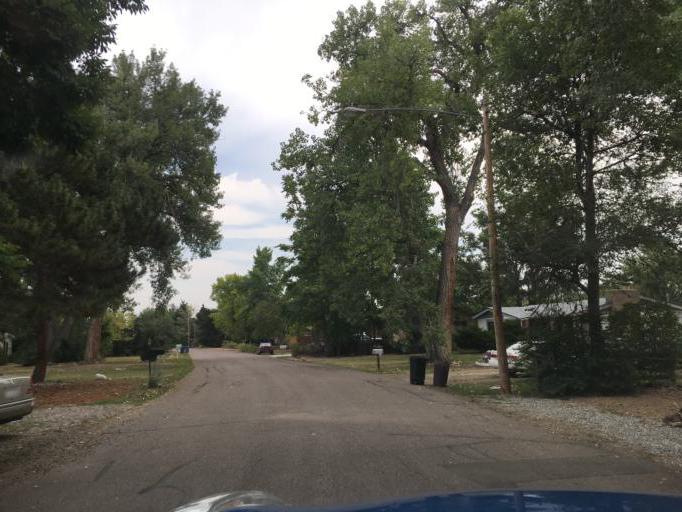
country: US
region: Colorado
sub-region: Jefferson County
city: Wheat Ridge
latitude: 39.7535
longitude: -105.0981
